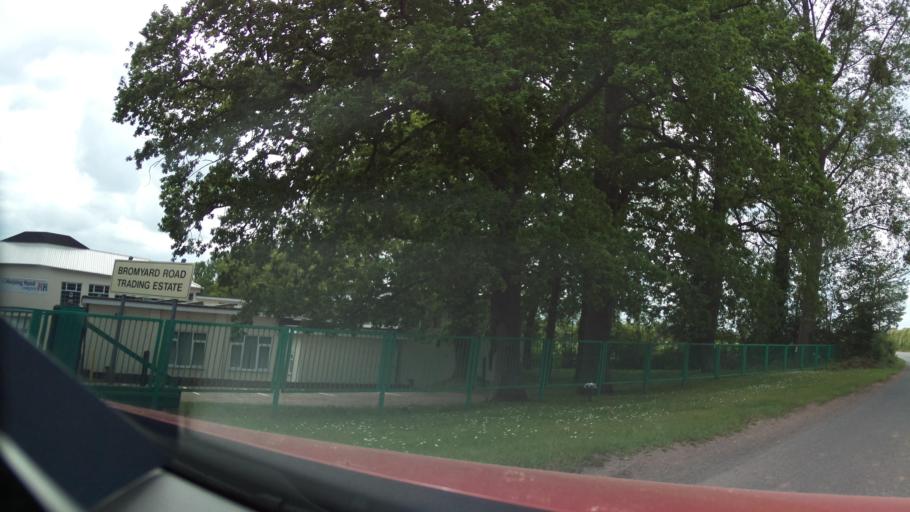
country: GB
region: England
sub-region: Herefordshire
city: Ledbury
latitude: 52.0511
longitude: -2.4336
